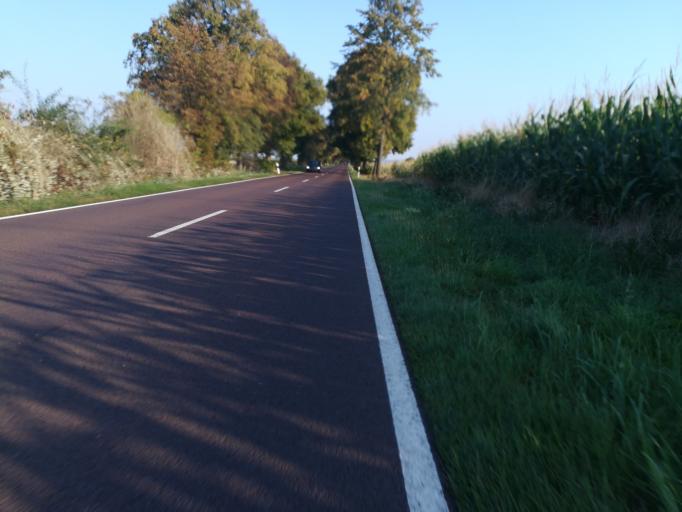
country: DE
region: Saxony-Anhalt
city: Haldensleben I
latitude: 52.2444
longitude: 11.4374
